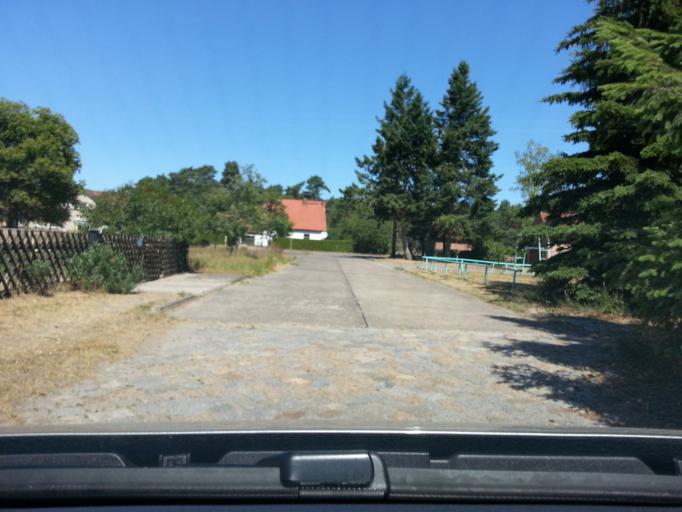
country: DE
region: Mecklenburg-Vorpommern
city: Viereck
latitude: 53.5729
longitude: 14.0130
